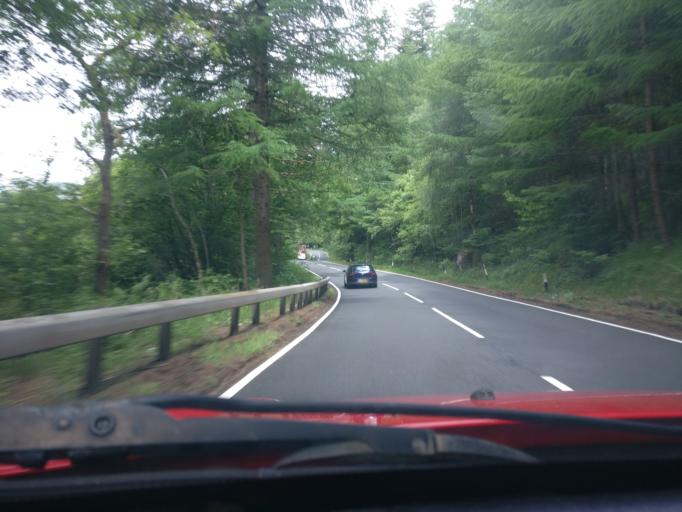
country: GB
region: Scotland
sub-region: Stirling
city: Callander
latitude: 56.2742
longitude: -4.2822
